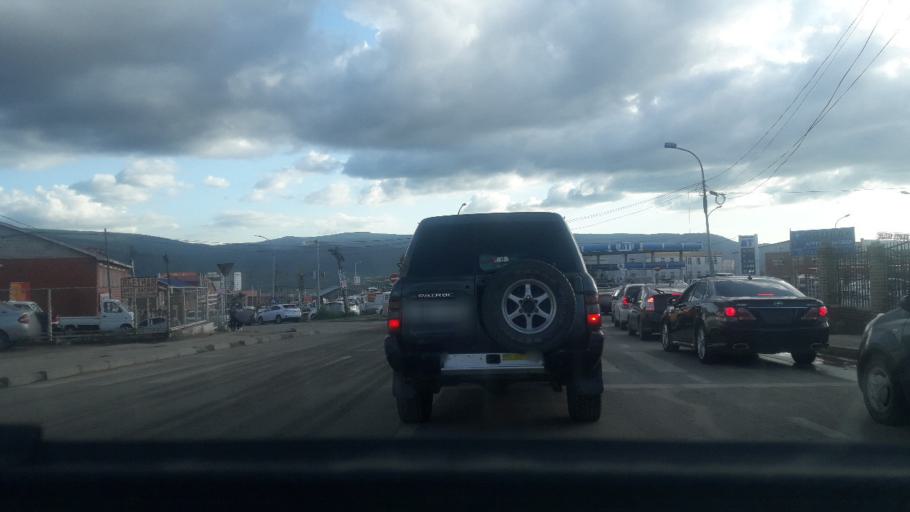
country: MN
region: Ulaanbaatar
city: Ulaanbaatar
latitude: 47.9246
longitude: 106.9967
